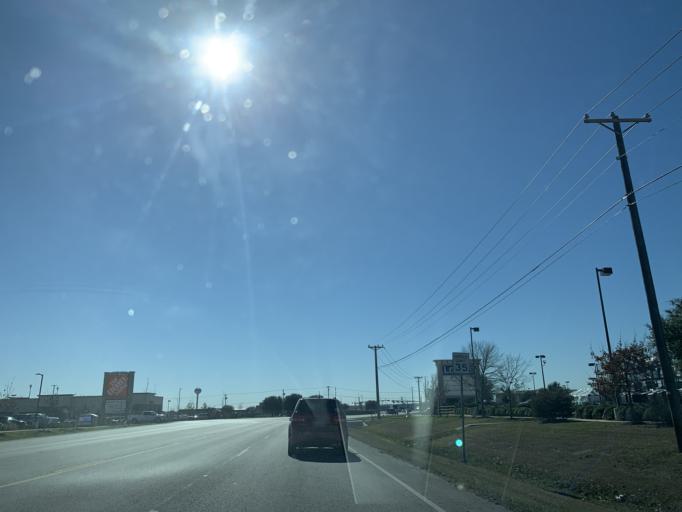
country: US
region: Texas
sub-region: Williamson County
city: Hutto
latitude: 30.5436
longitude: -97.5617
